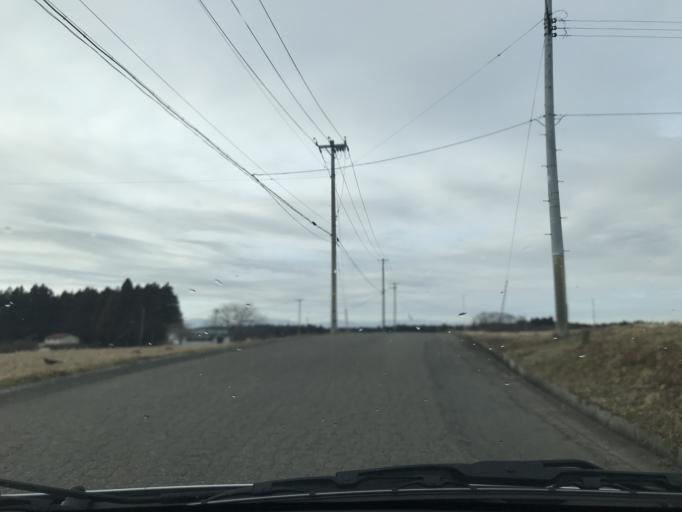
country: JP
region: Iwate
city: Kitakami
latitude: 39.2138
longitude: 141.0615
